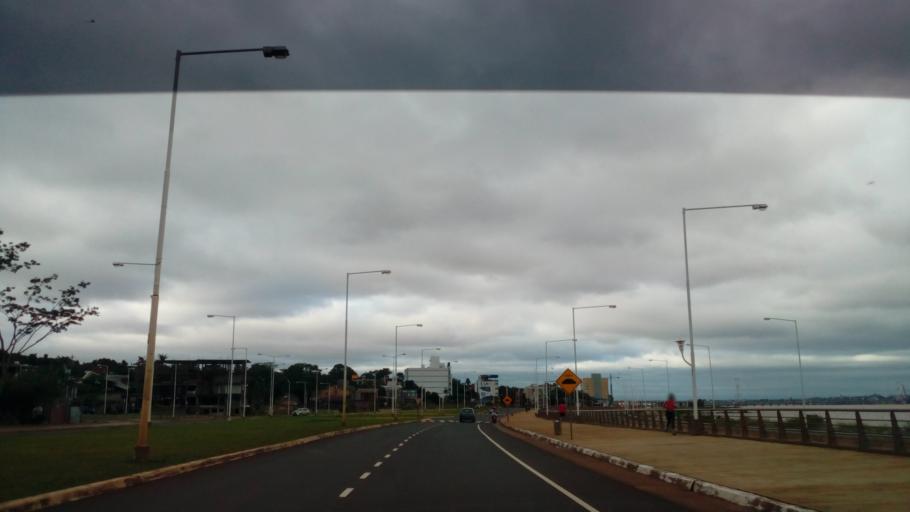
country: AR
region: Misiones
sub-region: Departamento de Capital
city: Posadas
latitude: -27.3935
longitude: -55.8925
